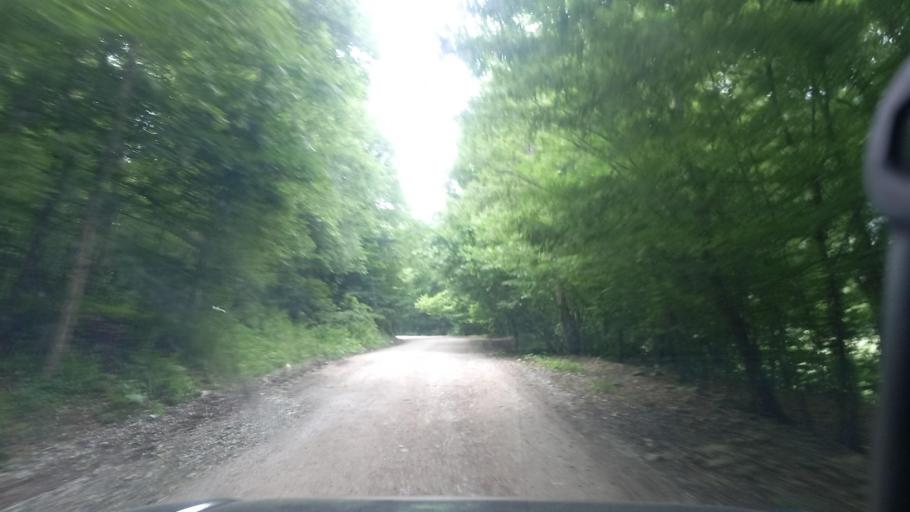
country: RU
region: Karachayevo-Cherkesiya
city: Kurdzhinovo
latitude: 43.8383
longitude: 40.9303
